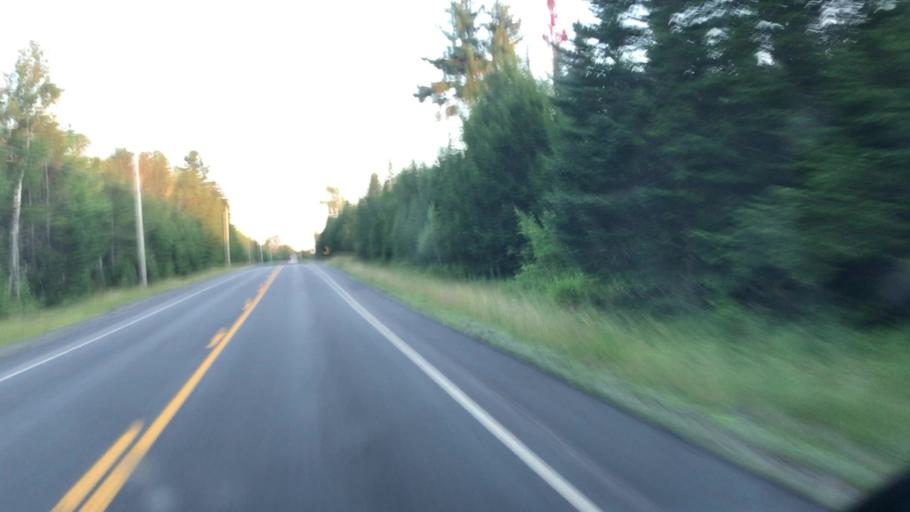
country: US
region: Maine
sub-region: Penobscot County
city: Medway
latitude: 45.5710
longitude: -68.3212
